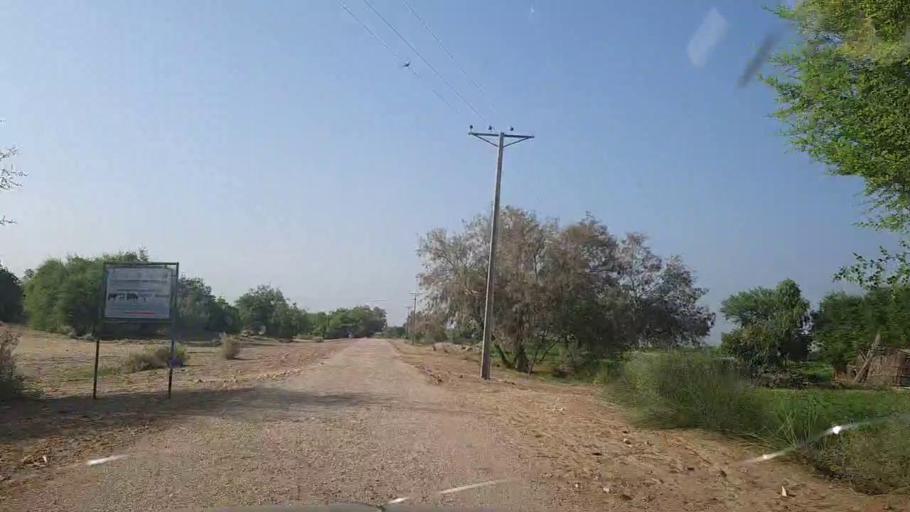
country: PK
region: Sindh
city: Khanpur
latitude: 27.7154
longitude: 69.3319
